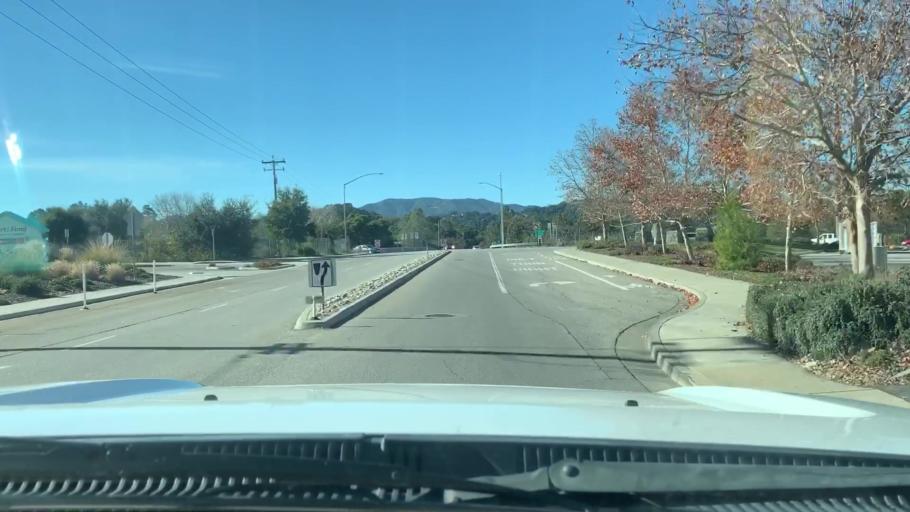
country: US
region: California
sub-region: San Luis Obispo County
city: Atascadero
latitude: 35.4773
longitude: -120.6569
